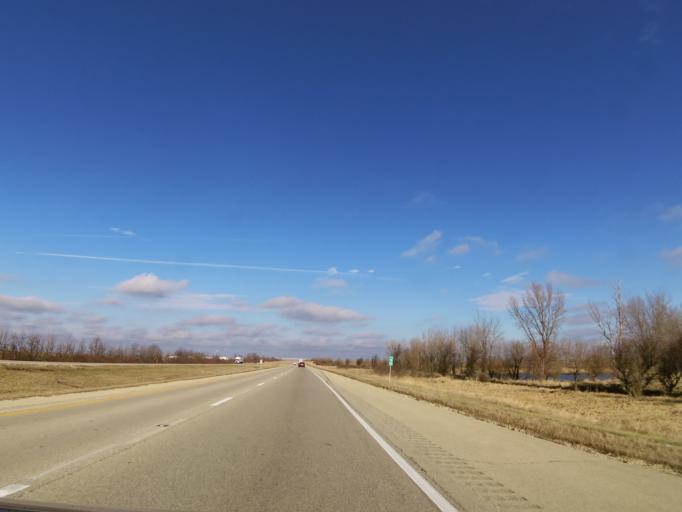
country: US
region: Illinois
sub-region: Ogle County
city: Rochelle
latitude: 41.8052
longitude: -89.0093
